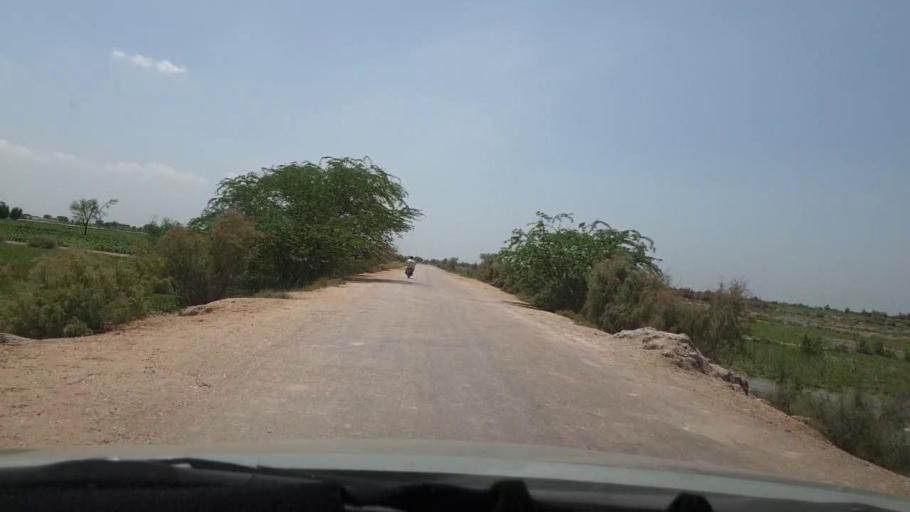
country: PK
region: Sindh
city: Pano Aqil
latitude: 27.6633
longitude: 69.1596
